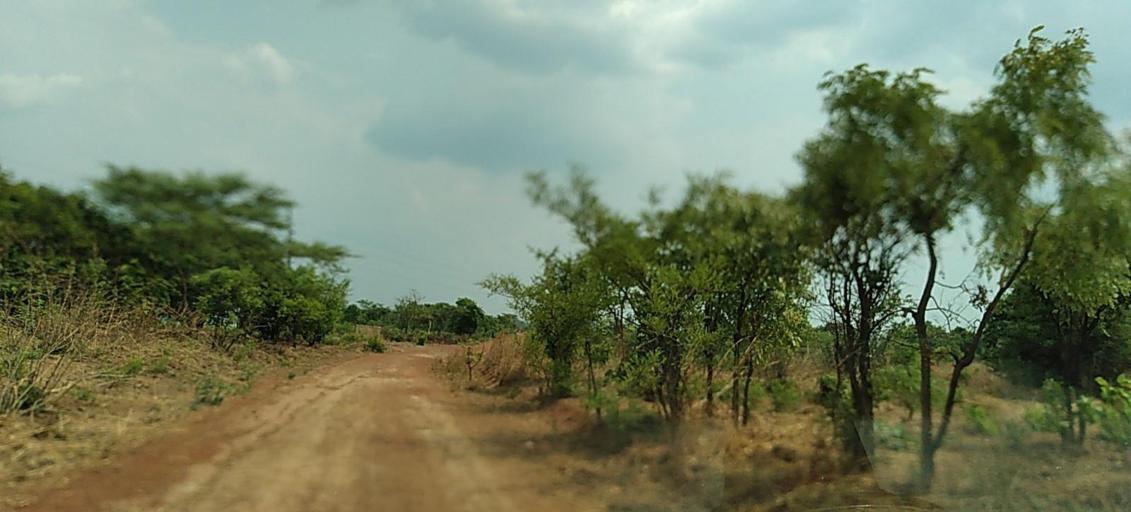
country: ZM
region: Copperbelt
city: Kalulushi
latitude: -12.8798
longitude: 28.0748
